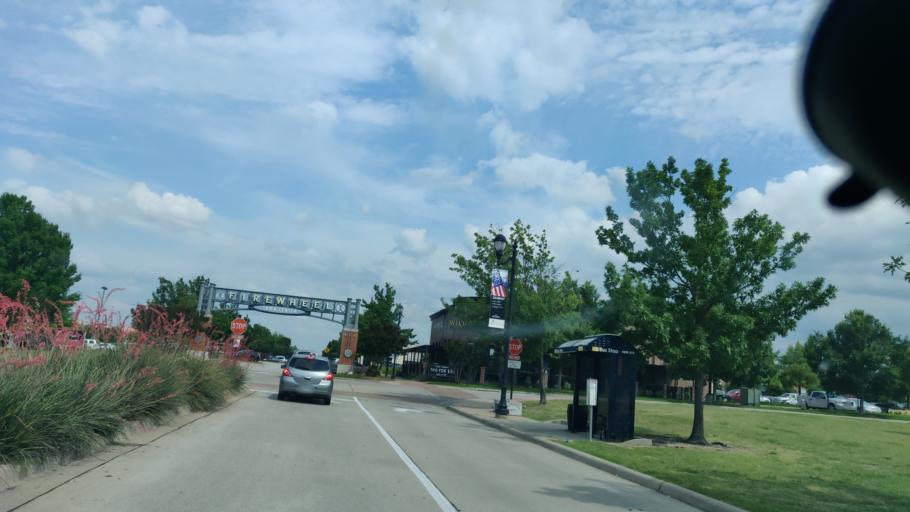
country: US
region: Texas
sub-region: Dallas County
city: Sachse
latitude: 32.9535
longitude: -96.6153
